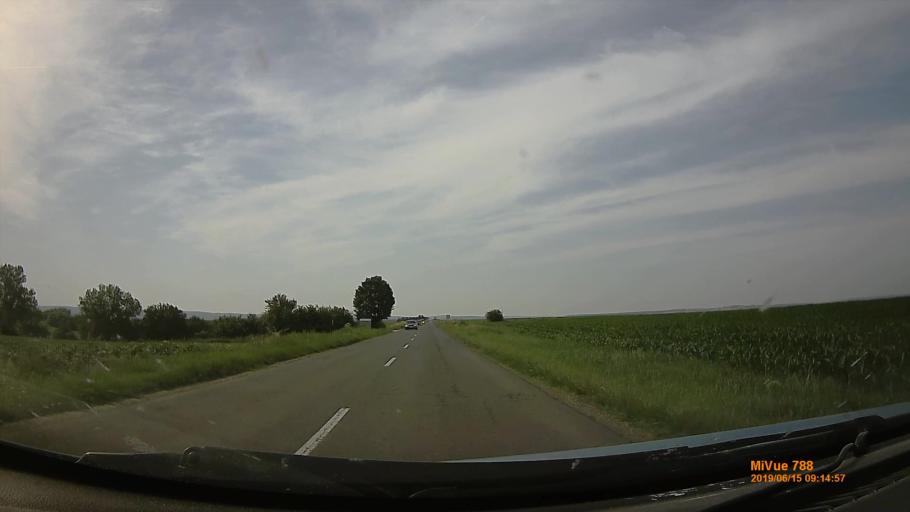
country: HU
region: Tolna
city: Iregszemcse
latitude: 46.6364
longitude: 18.1985
